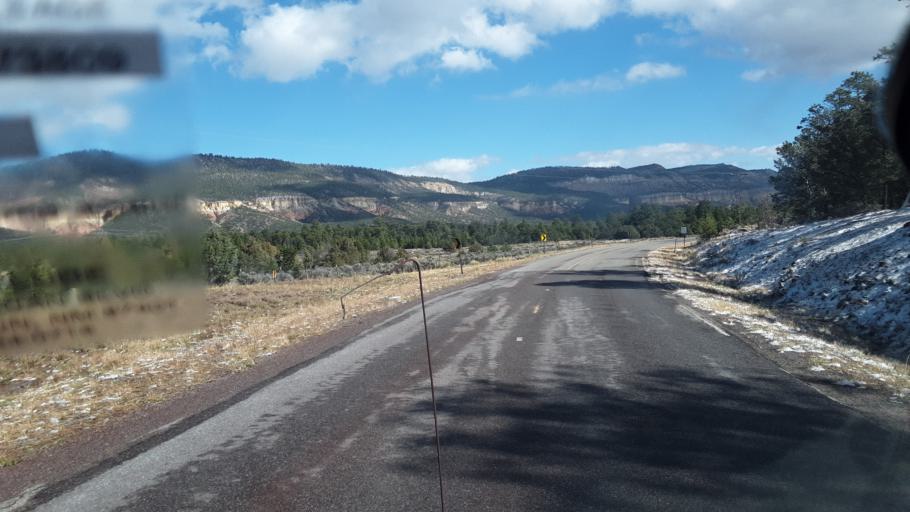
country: US
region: New Mexico
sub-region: Rio Arriba County
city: Santa Teresa
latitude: 36.2001
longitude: -106.7367
